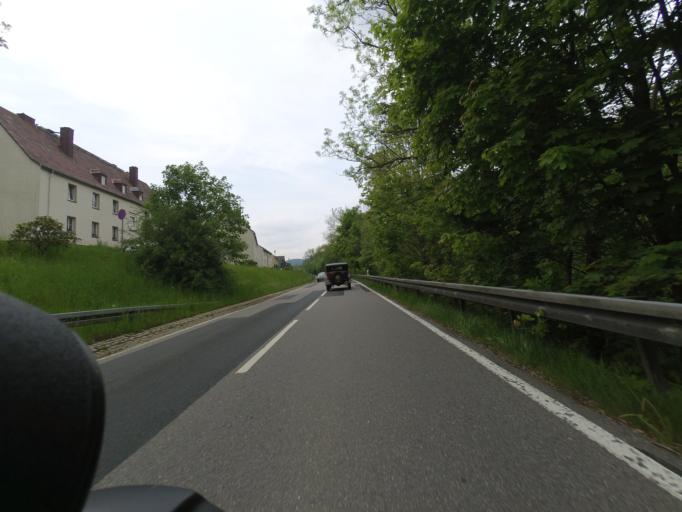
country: DE
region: Saxony
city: Scharfenstein
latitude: 50.6944
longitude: 13.0616
